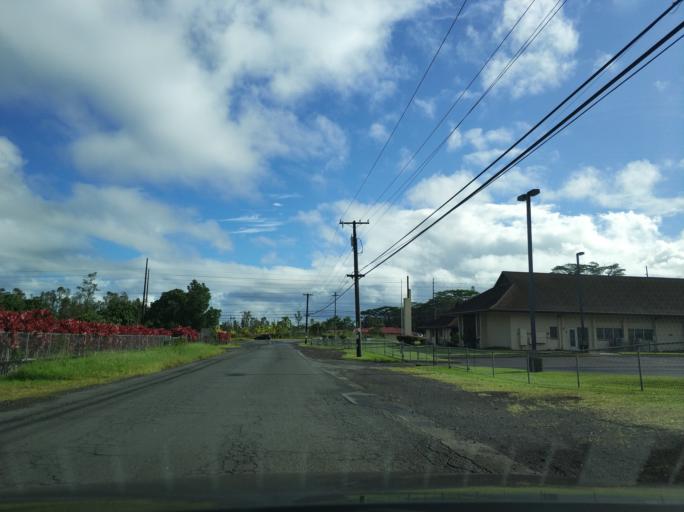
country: US
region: Hawaii
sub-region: Hawaii County
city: Orchidlands Estates
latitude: 19.5597
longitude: -154.9934
